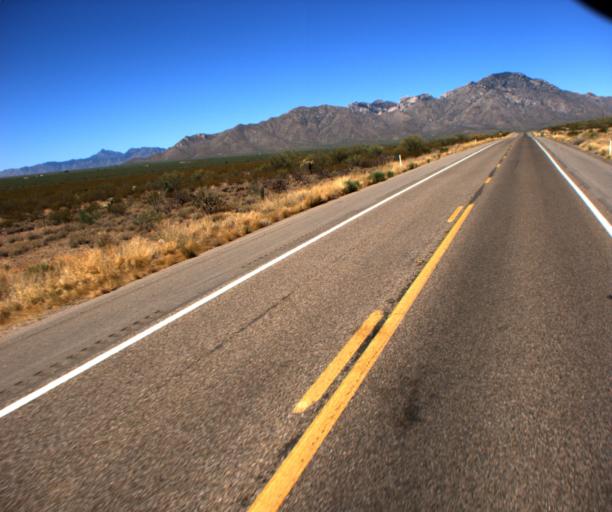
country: US
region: Arizona
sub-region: Pima County
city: Three Points
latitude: 32.0464
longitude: -111.4307
